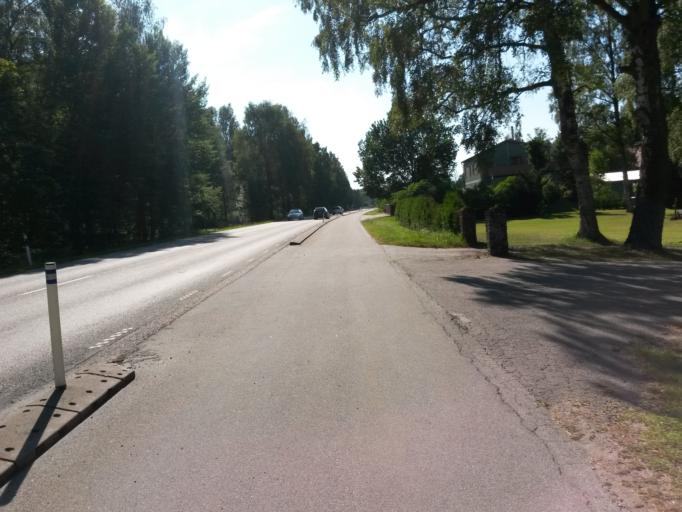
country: SE
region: Vaestra Goetaland
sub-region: Lidkopings Kommun
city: Vinninga
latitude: 58.4927
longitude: 13.2560
